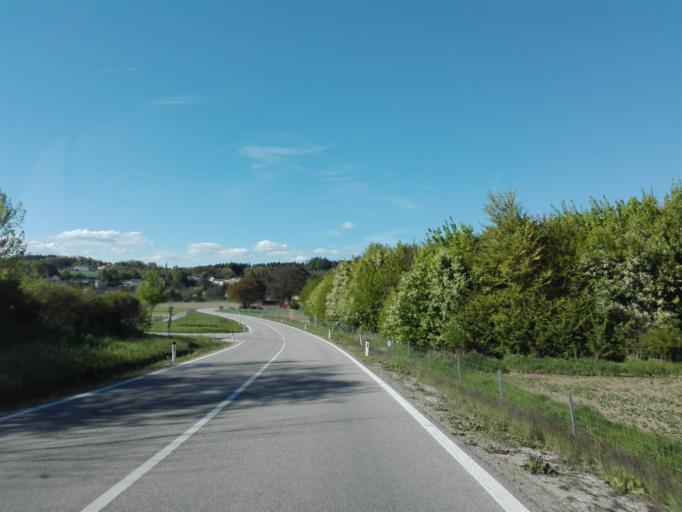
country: AT
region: Upper Austria
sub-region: Politischer Bezirk Perg
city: Perg
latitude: 48.2435
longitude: 14.6492
